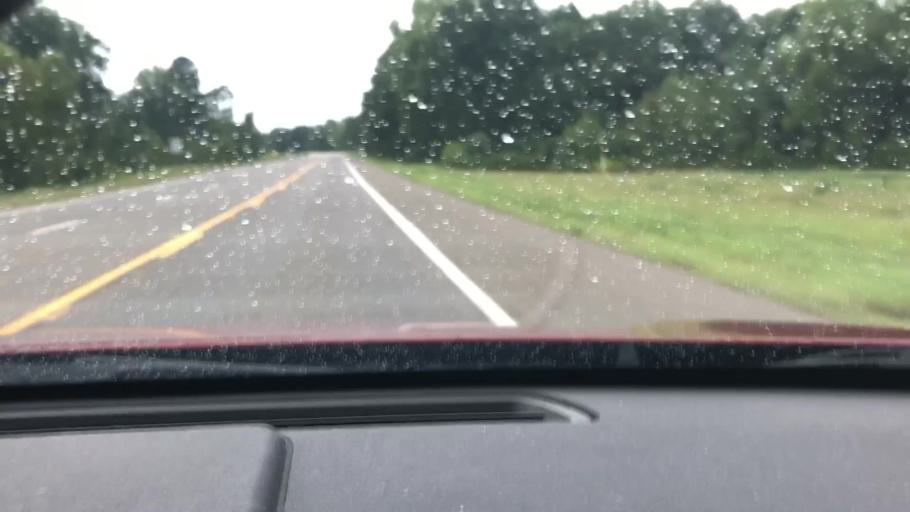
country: US
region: Arkansas
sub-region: Lafayette County
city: Stamps
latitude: 33.3640
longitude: -93.4704
